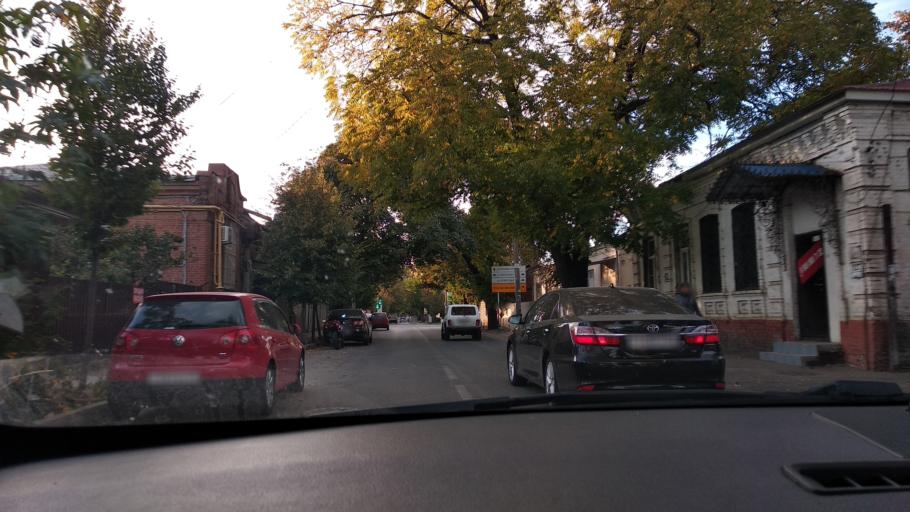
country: RU
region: Krasnodarskiy
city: Krasnodar
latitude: 45.0265
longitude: 38.9833
